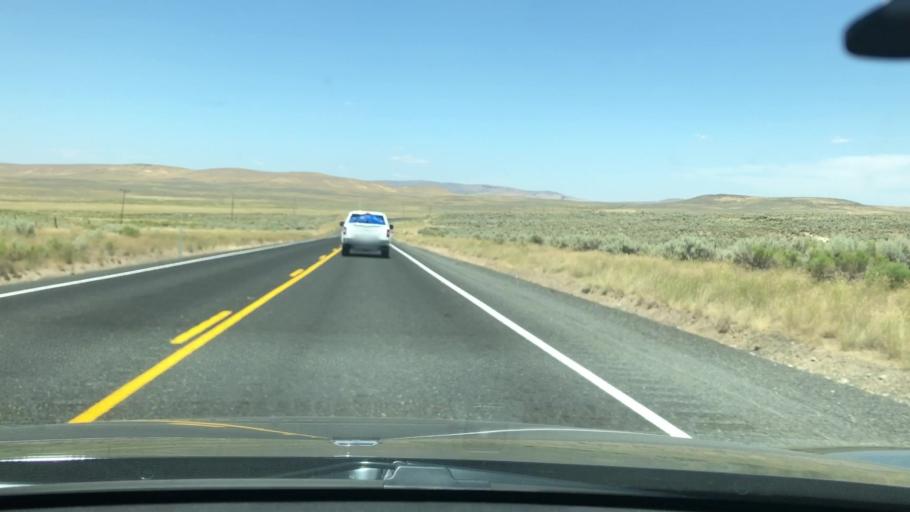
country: US
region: Idaho
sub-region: Owyhee County
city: Murphy
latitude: 43.0352
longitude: -117.0687
